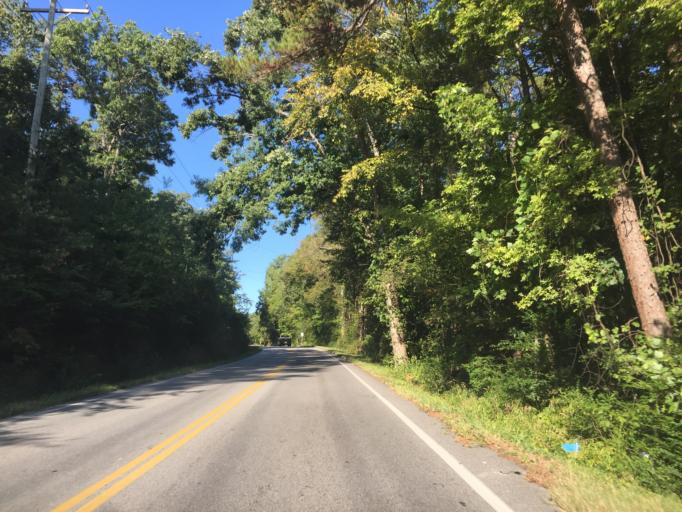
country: US
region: Tennessee
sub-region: Hamilton County
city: Harrison
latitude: 35.1216
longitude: -85.1009
